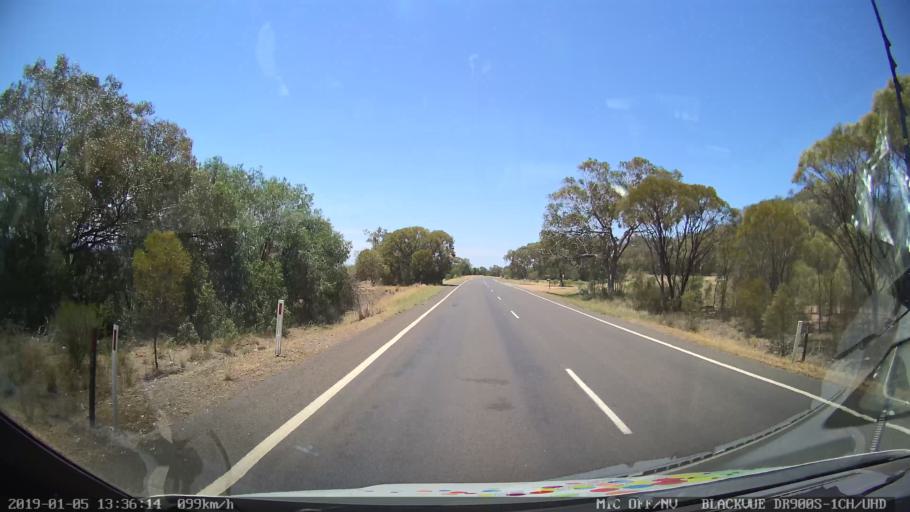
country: AU
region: New South Wales
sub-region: Gunnedah
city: Gunnedah
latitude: -30.9863
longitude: 150.1616
